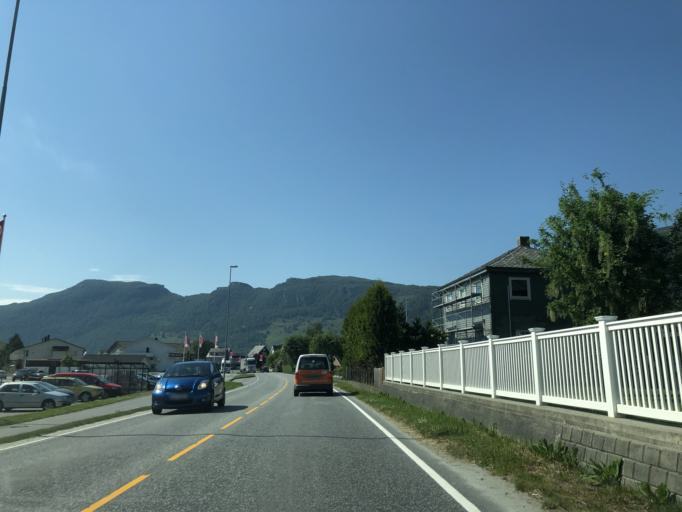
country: NO
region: Hordaland
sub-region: Etne
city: Etne
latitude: 59.6646
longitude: 5.9416
